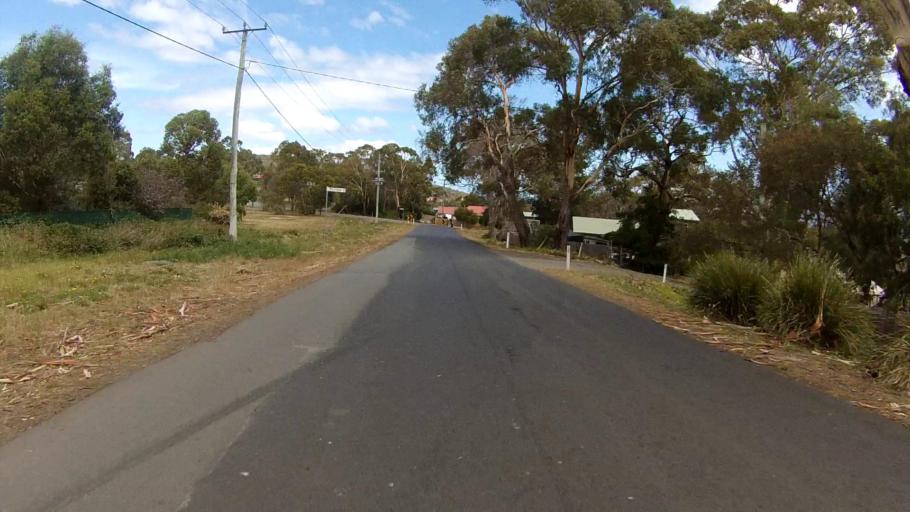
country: AU
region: Tasmania
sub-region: Sorell
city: Sorell
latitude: -42.8687
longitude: 147.6442
